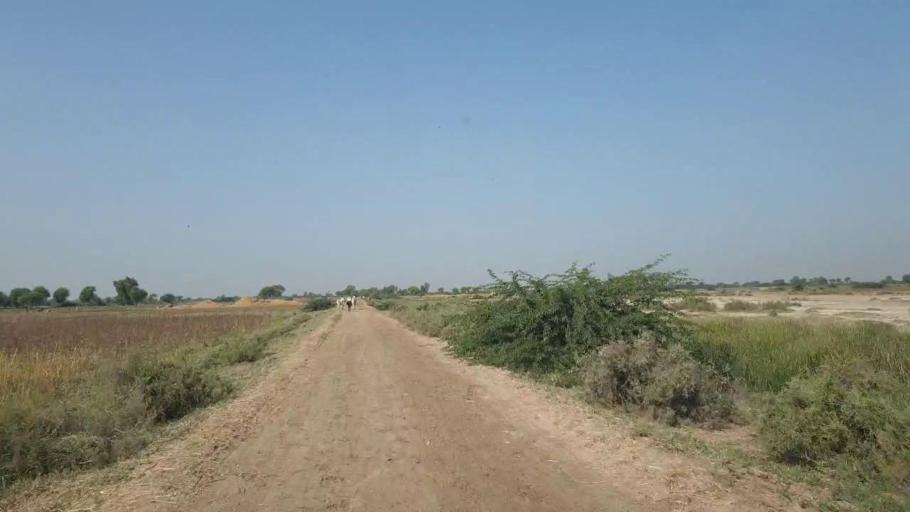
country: PK
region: Sindh
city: Badin
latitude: 24.5236
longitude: 68.7537
